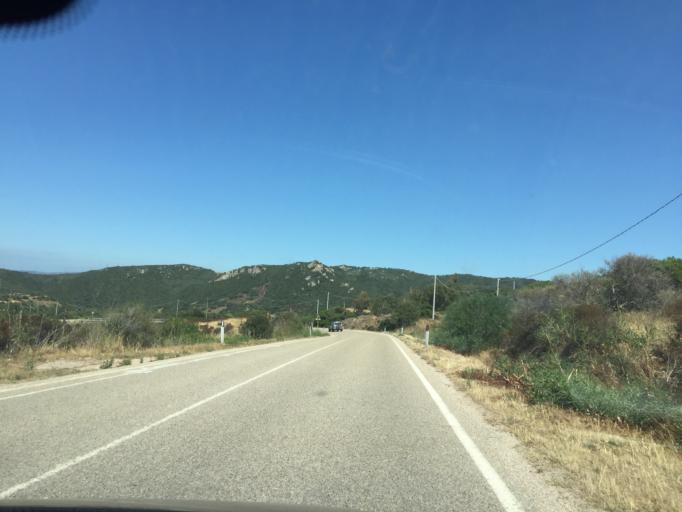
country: IT
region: Sardinia
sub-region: Provincia di Olbia-Tempio
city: Aglientu
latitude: 41.0949
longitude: 9.0987
